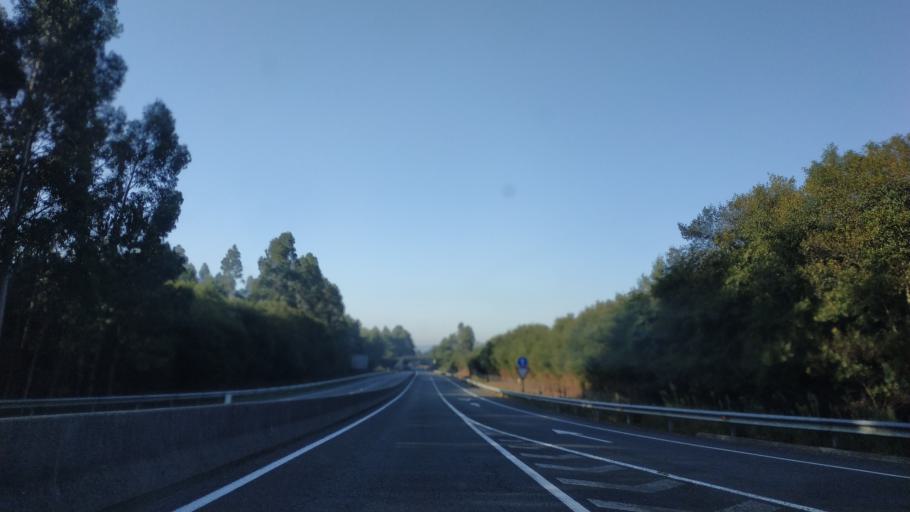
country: ES
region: Galicia
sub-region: Provincia da Coruna
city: Carballo
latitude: 43.2444
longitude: -8.6748
